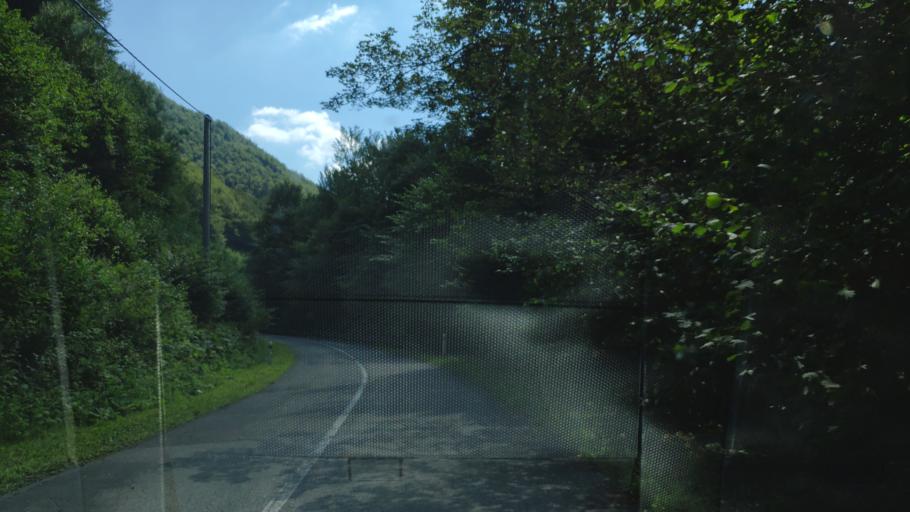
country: PL
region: Subcarpathian Voivodeship
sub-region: Powiat leski
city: Cisna
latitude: 49.0677
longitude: 22.3626
